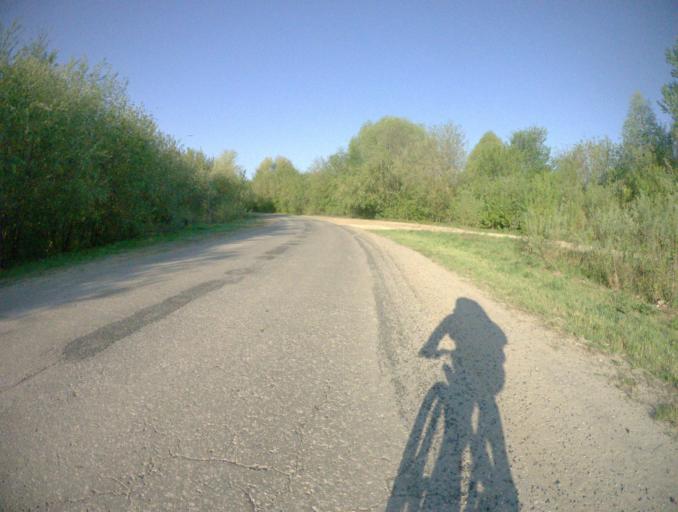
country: RU
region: Vladimir
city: Vyazniki
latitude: 56.2512
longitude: 42.1714
